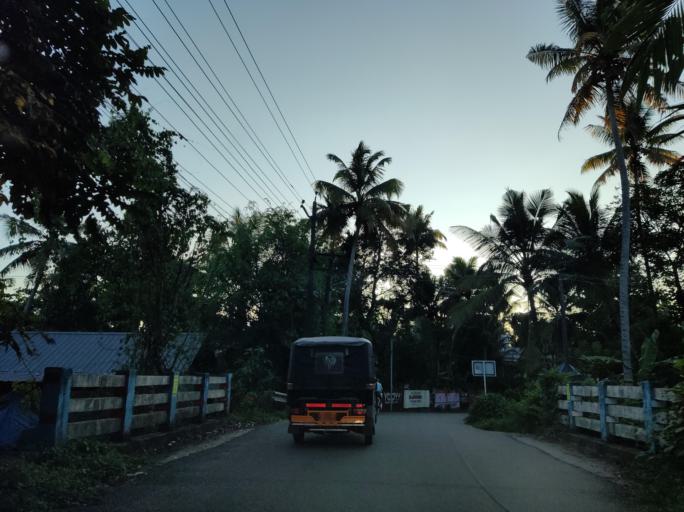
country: IN
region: Kerala
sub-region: Alappuzha
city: Vayalar
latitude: 9.7061
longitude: 76.2996
